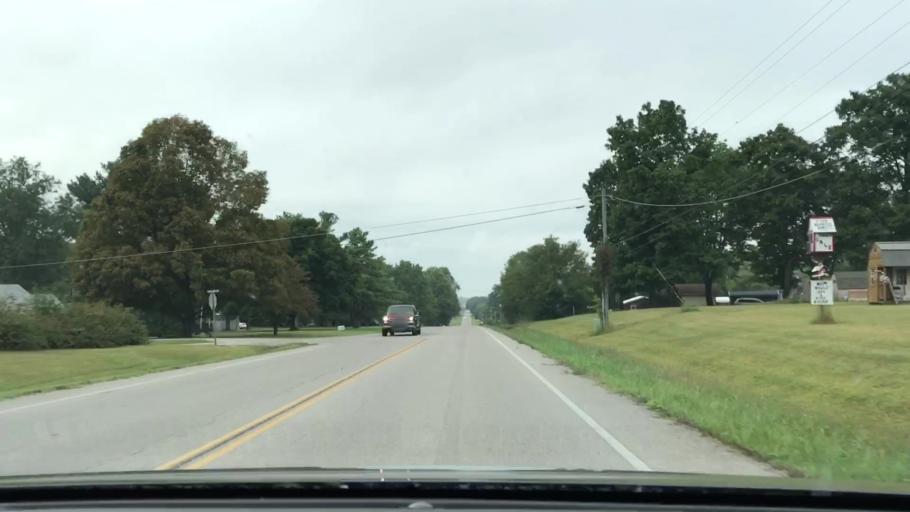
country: US
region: Tennessee
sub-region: Sumner County
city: Portland
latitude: 36.5169
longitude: -86.5008
